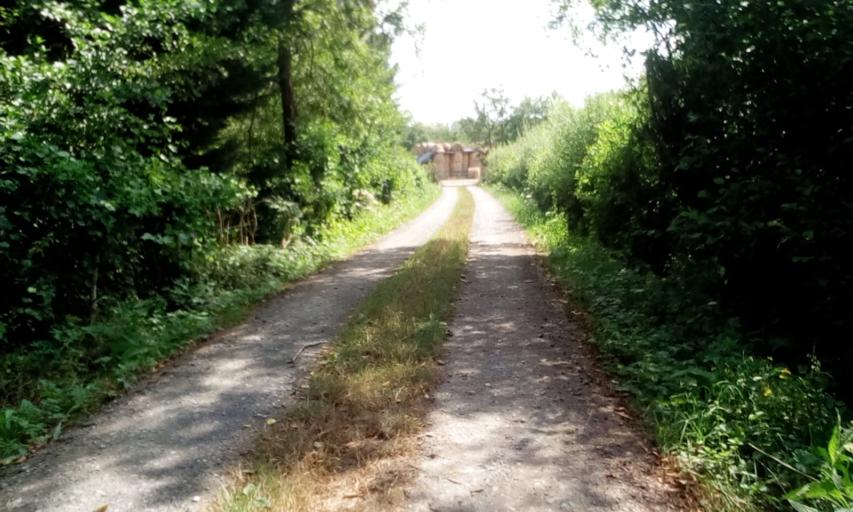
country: FR
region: Lower Normandy
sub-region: Departement du Calvados
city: Bavent
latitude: 49.2405
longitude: -0.1714
